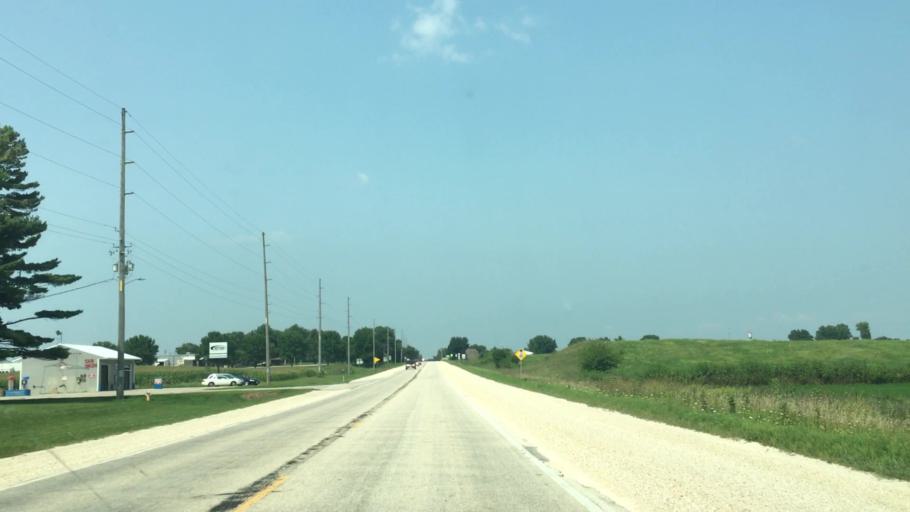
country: US
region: Iowa
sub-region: Fayette County
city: West Union
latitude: 42.9452
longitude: -91.8142
